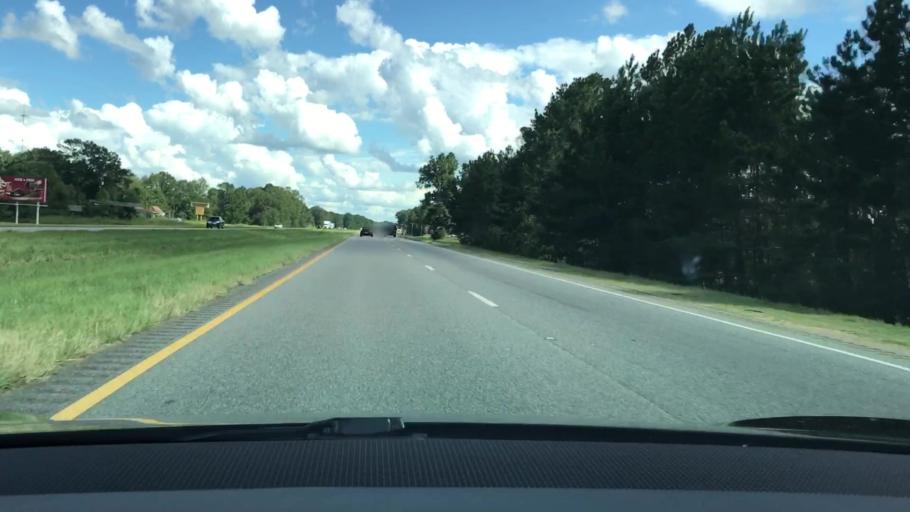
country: US
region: Alabama
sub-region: Montgomery County
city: Taylor
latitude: 32.0510
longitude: -86.0429
